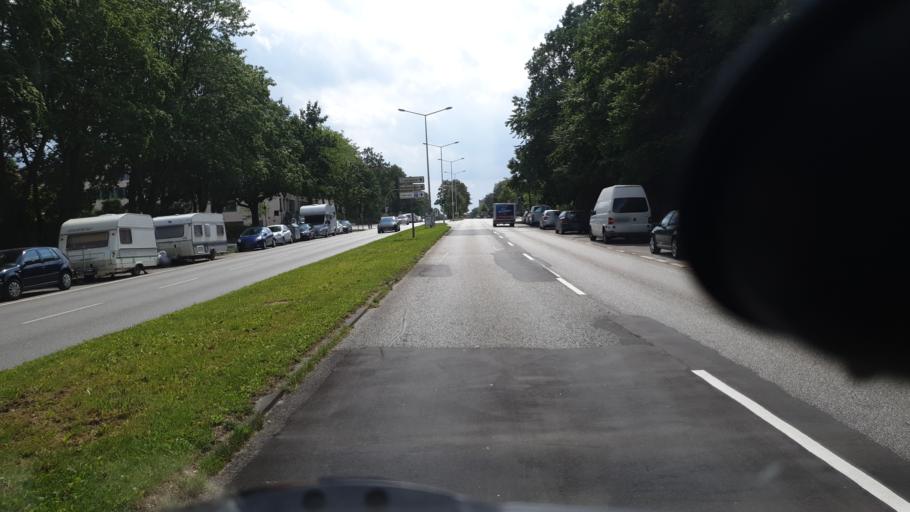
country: DE
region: Schleswig-Holstein
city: Kiel
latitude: 54.3433
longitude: 10.1276
